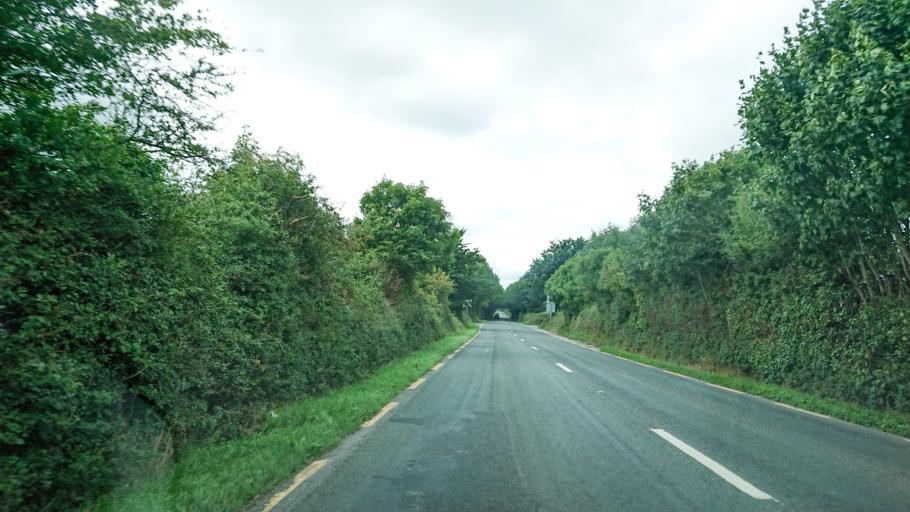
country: IE
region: Munster
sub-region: Waterford
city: Dungarvan
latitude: 52.1101
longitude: -7.6830
